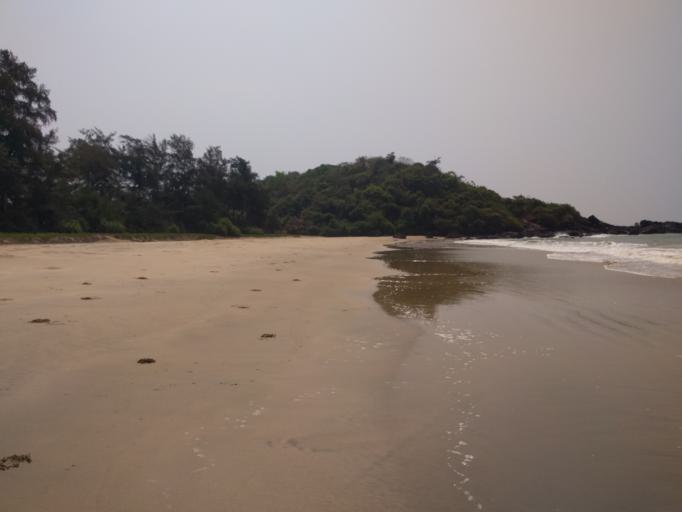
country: IN
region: Karnataka
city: Canacona
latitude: 14.9750
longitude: 74.0431
